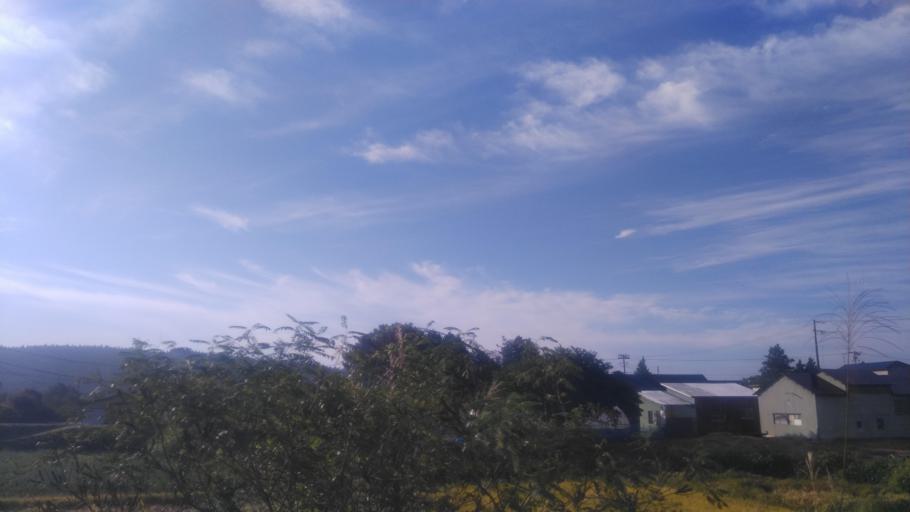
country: JP
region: Akita
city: Takanosu
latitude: 40.2576
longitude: 140.4009
